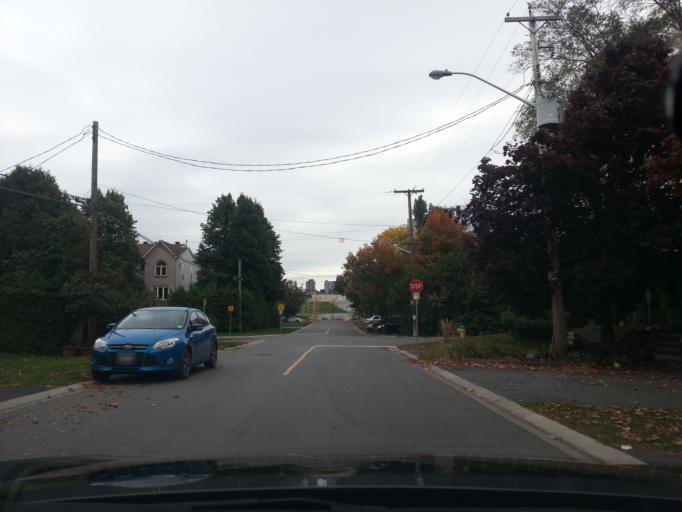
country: CA
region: Ontario
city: Ottawa
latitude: 45.3839
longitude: -75.7443
